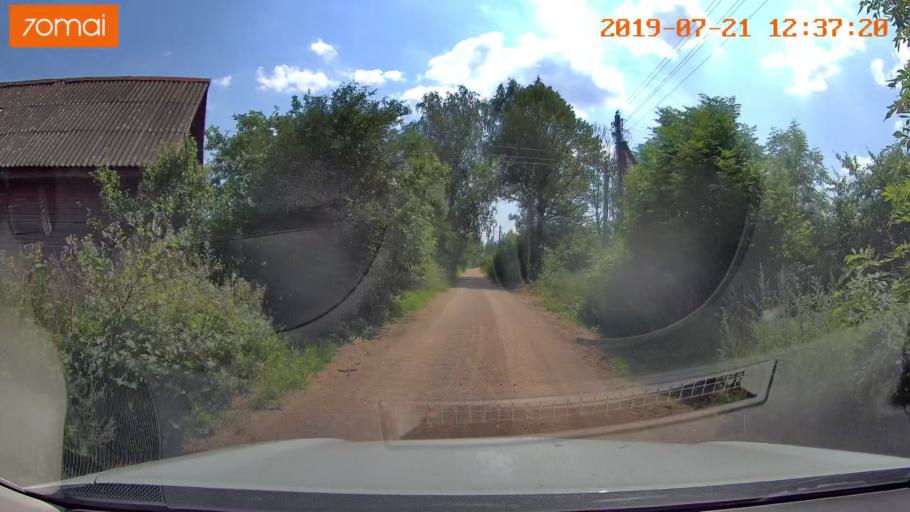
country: BY
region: Grodnenskaya
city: Lyubcha
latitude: 53.8646
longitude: 26.0051
